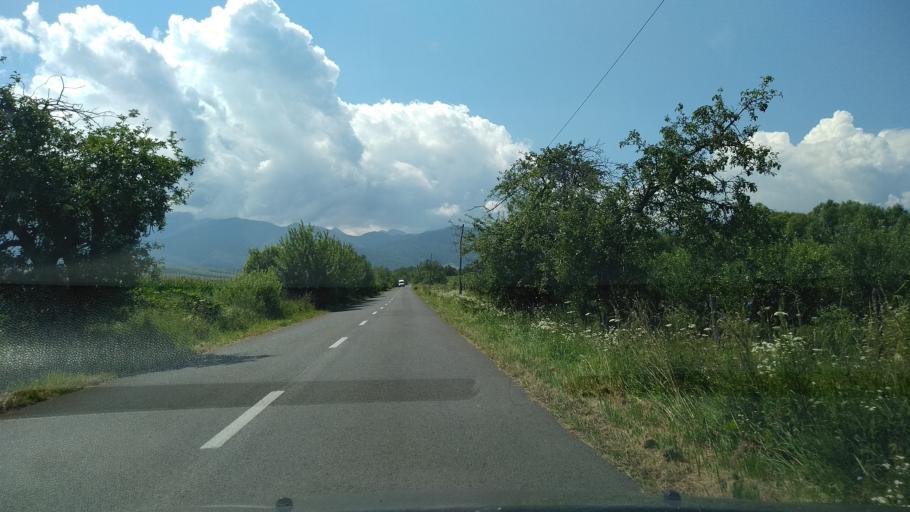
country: RO
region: Hunedoara
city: Salasu de Sus
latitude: 45.5201
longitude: 22.9610
